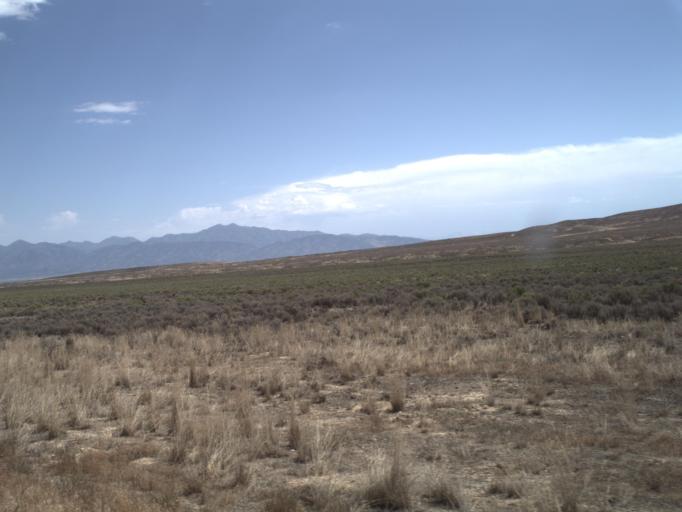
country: US
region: Utah
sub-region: Tooele County
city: Tooele
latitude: 40.1283
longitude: -112.4308
